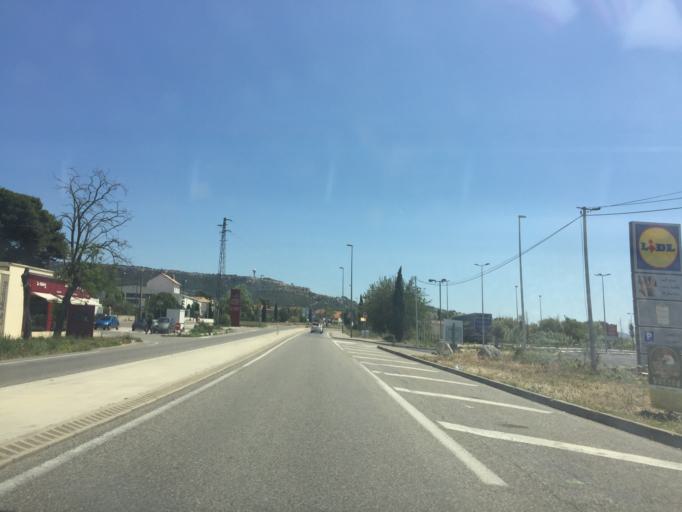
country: FR
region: Provence-Alpes-Cote d'Azur
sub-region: Departement des Bouches-du-Rhone
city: Rognac
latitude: 43.4866
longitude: 5.2215
